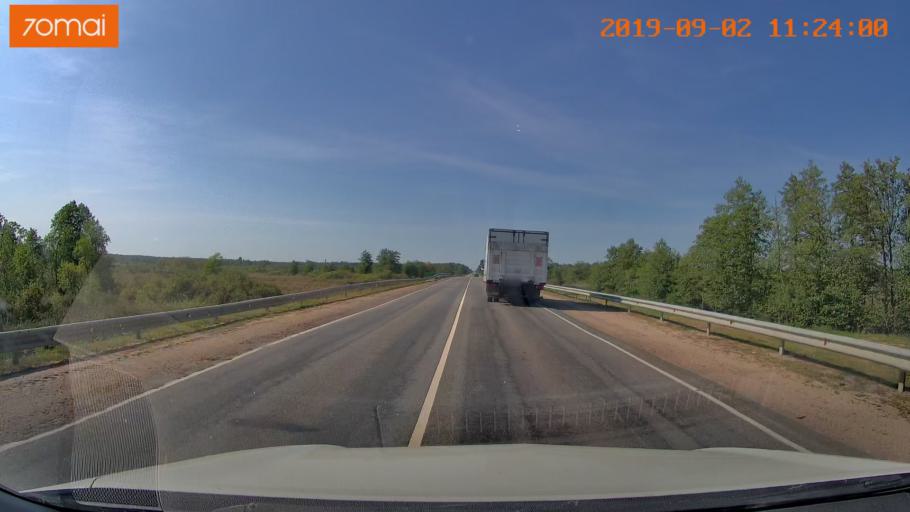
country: RU
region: Smolensk
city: Roslavl'
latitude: 54.0133
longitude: 32.9825
